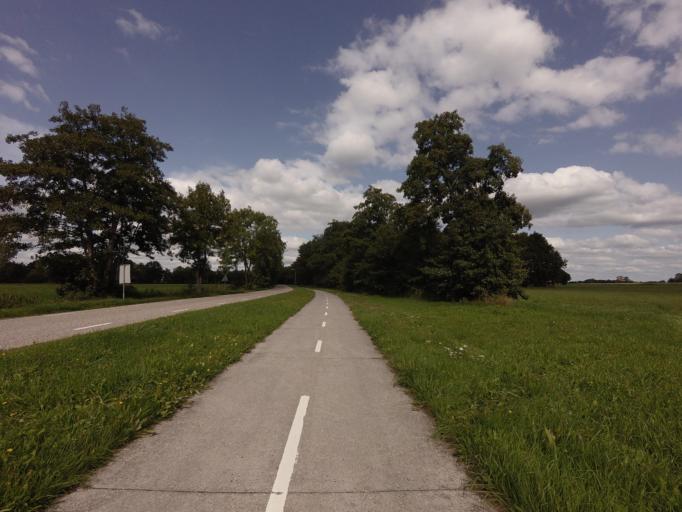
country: NL
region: Drenthe
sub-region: Gemeente De Wolden
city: Ruinen
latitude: 52.6856
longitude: 6.3001
